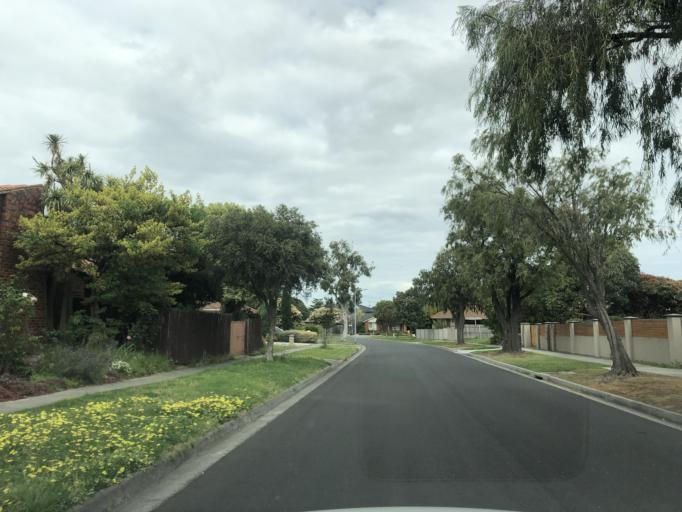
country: AU
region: Victoria
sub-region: Greater Dandenong
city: Noble Park North
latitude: -37.9361
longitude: 145.1971
